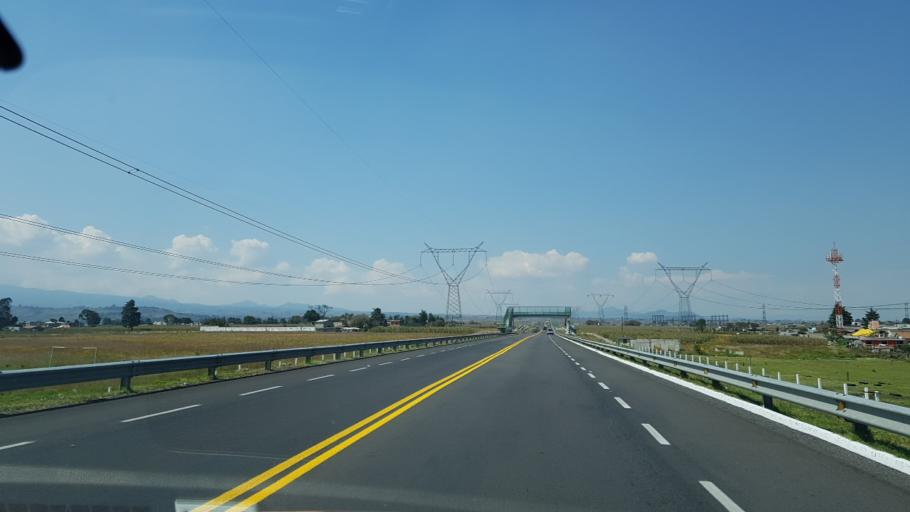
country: MX
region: Mexico
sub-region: Almoloya de Juarez
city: Fraccionamiento Colinas del Sol
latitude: 19.3863
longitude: -99.7478
